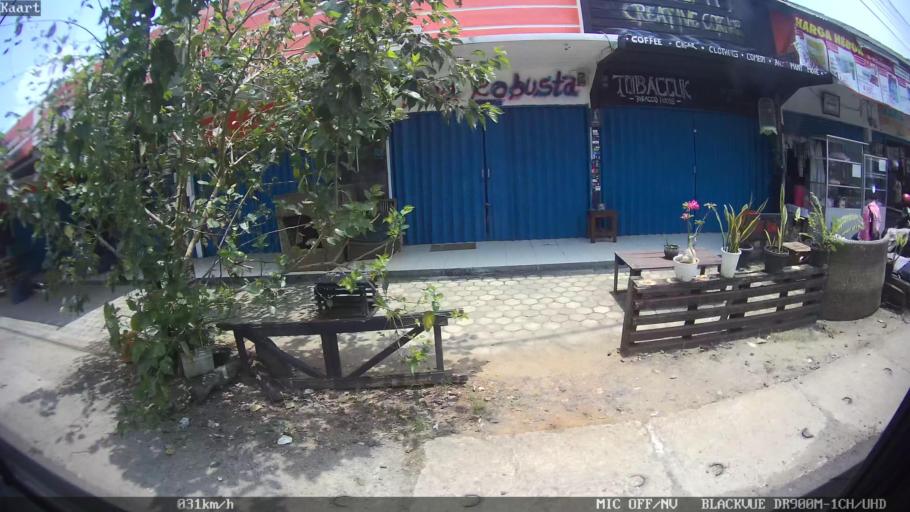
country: ID
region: Lampung
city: Kedaton
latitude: -5.3586
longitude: 105.2361
